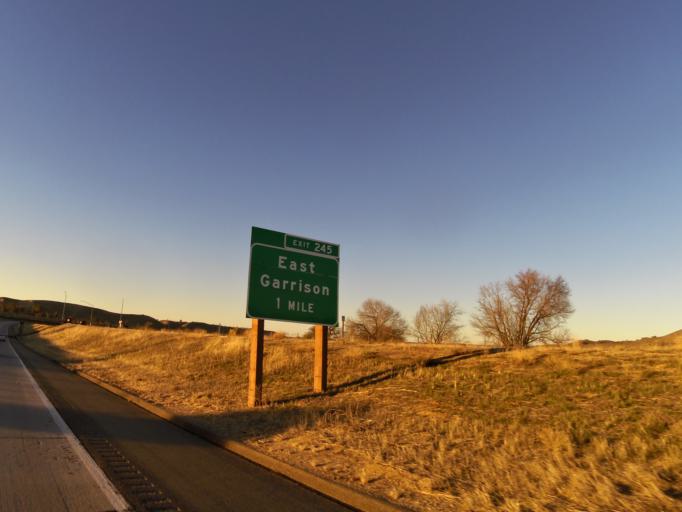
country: US
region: California
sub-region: San Luis Obispo County
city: San Miguel
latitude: 35.7982
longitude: -120.7411
